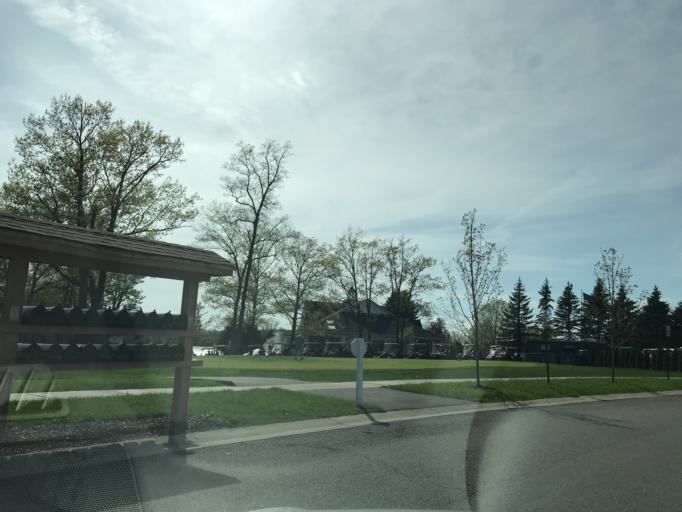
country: US
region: Michigan
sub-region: Oakland County
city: South Lyon
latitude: 42.4550
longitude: -83.5771
